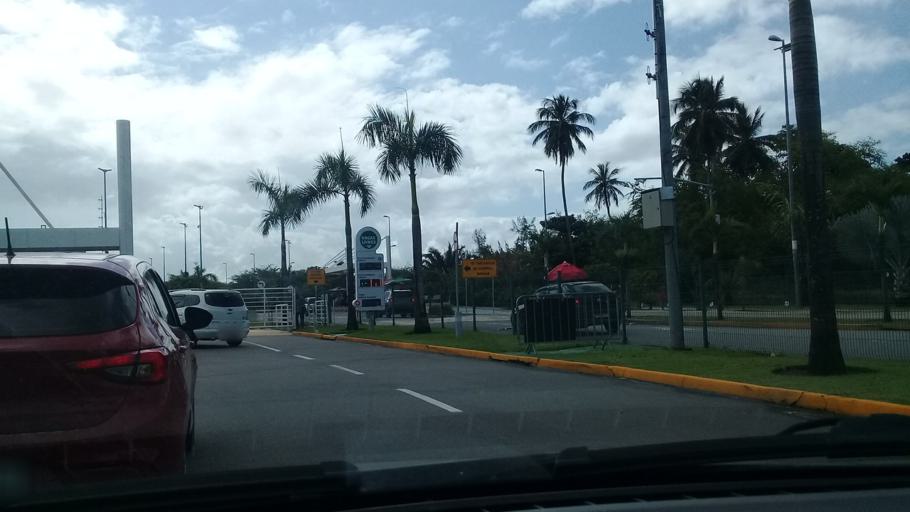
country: BR
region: Pernambuco
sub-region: Recife
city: Recife
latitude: -8.0847
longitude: -34.8945
